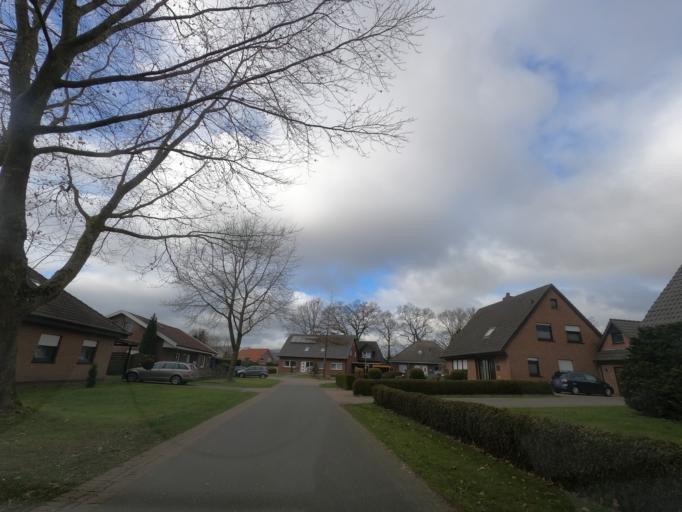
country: DE
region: Lower Saxony
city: Herzlake
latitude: 52.6890
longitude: 7.5912
